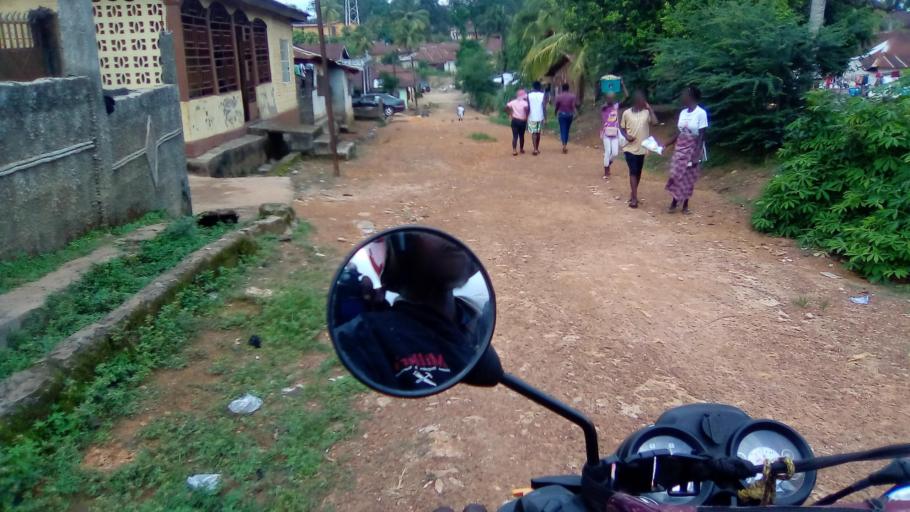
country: SL
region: Southern Province
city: Bo
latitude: 7.9582
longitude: -11.7316
